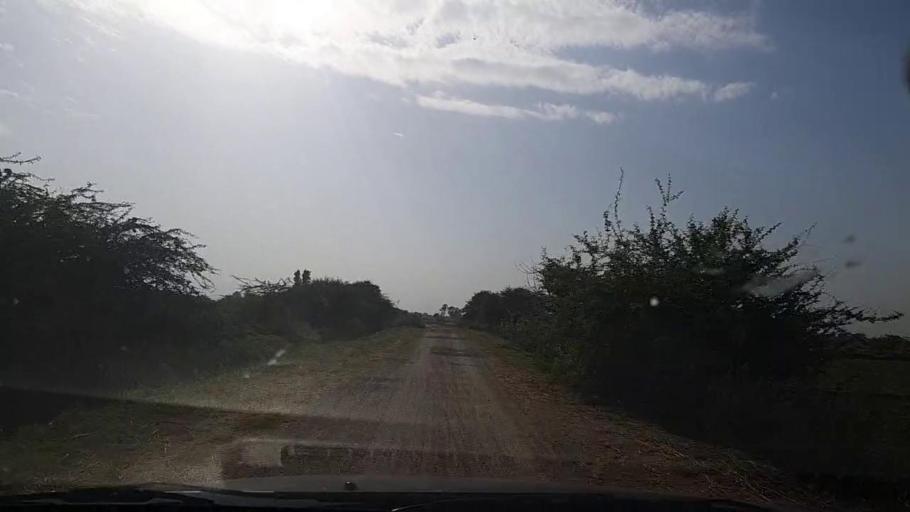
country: PK
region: Sindh
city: Mirpur Batoro
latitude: 24.5553
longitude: 68.1841
